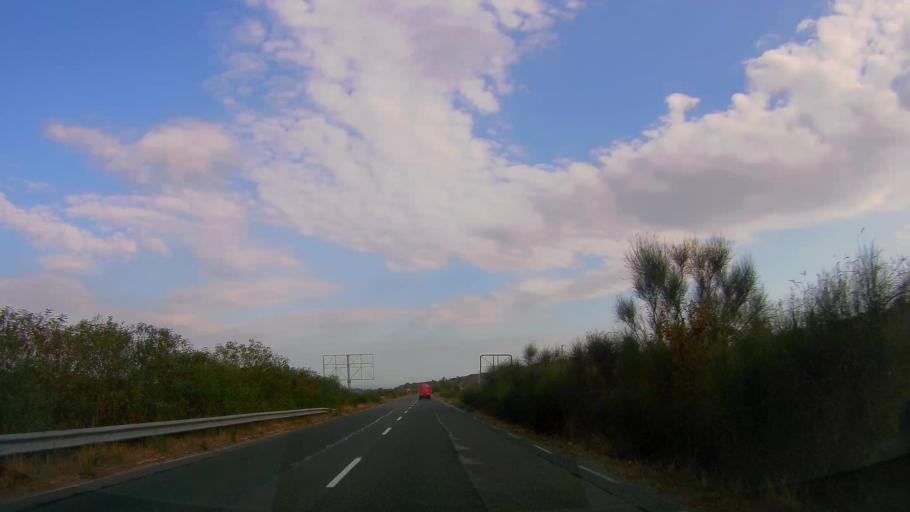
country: BG
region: Burgas
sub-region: Obshtina Sozopol
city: Sozopol
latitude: 42.3742
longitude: 27.6827
